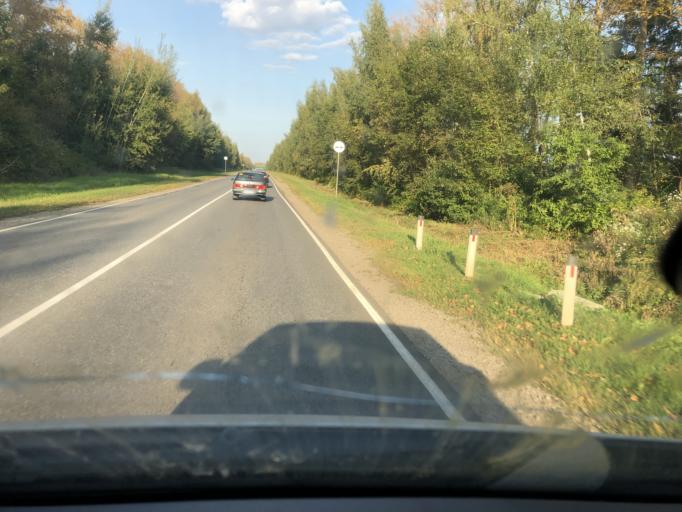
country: RU
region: Kaluga
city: Peremyshl'
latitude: 54.2430
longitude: 36.0790
